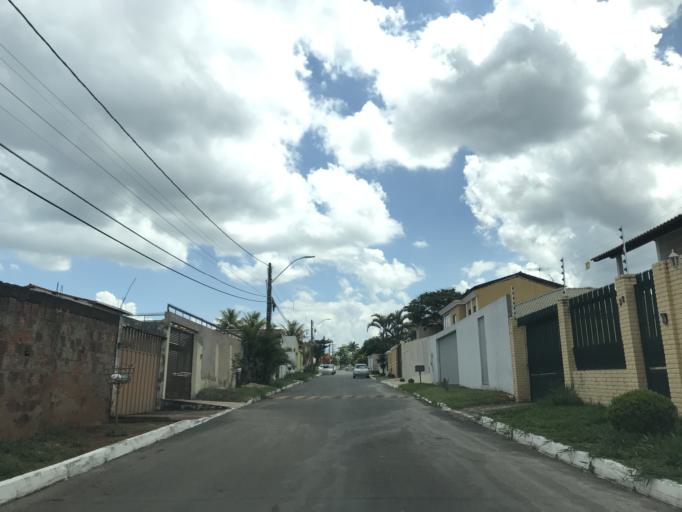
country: BR
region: Federal District
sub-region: Brasilia
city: Brasilia
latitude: -15.6823
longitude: -47.8347
